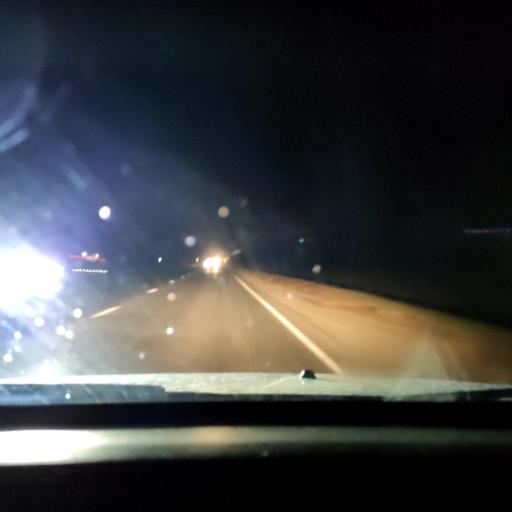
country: RU
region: Samara
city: Tol'yatti
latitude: 53.5823
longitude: 49.3346
